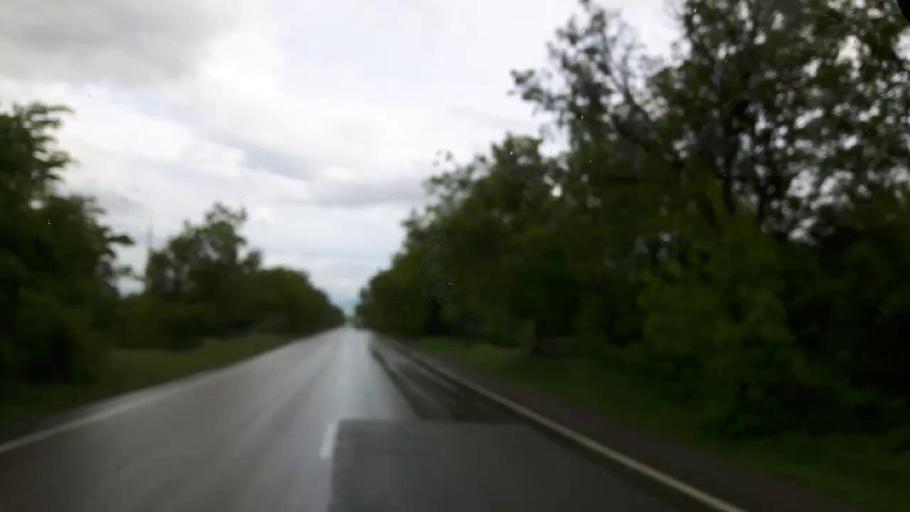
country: GE
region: Shida Kartli
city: Kaspi
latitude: 41.9697
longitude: 44.4560
